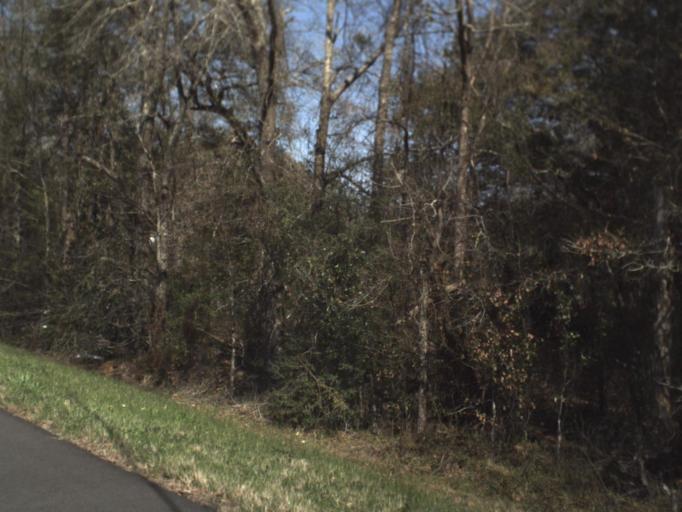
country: US
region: Florida
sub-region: Jackson County
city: Sneads
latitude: 30.7864
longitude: -85.0198
